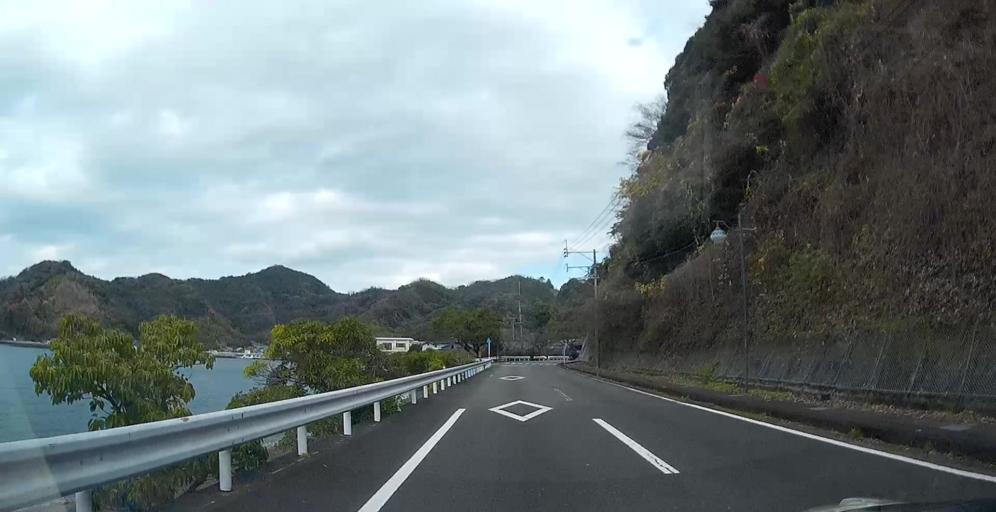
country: JP
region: Kumamoto
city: Minamata
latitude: 32.3287
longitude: 130.4835
